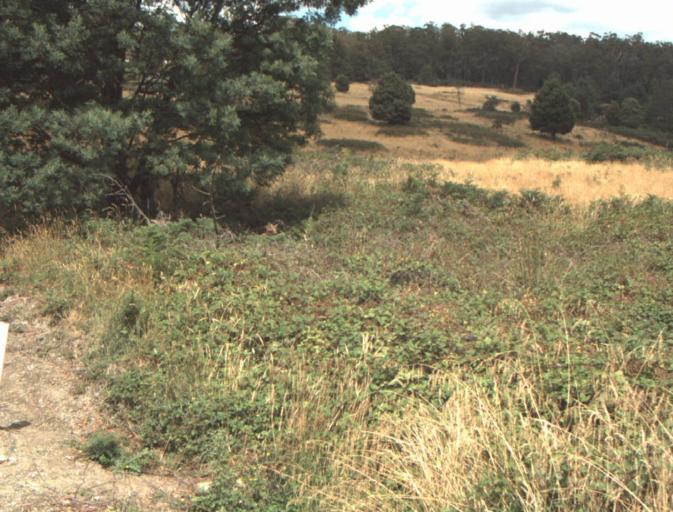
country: AU
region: Tasmania
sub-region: Launceston
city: Mayfield
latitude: -41.1964
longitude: 147.1698
